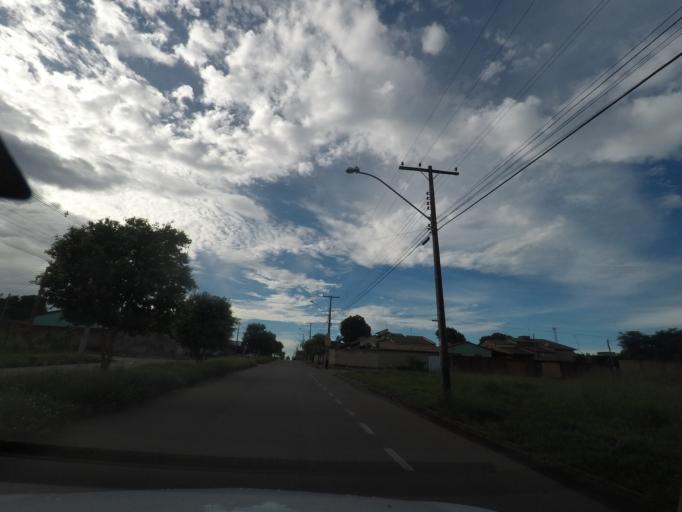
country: BR
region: Goias
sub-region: Aparecida De Goiania
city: Aparecida de Goiania
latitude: -16.7867
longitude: -49.3730
